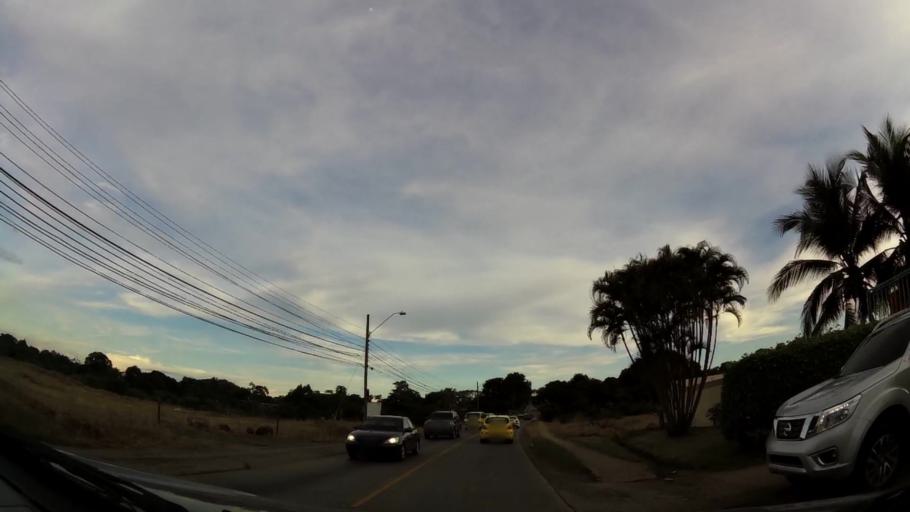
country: PA
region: Panama
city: La Chorrera
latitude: 8.8714
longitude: -79.7730
